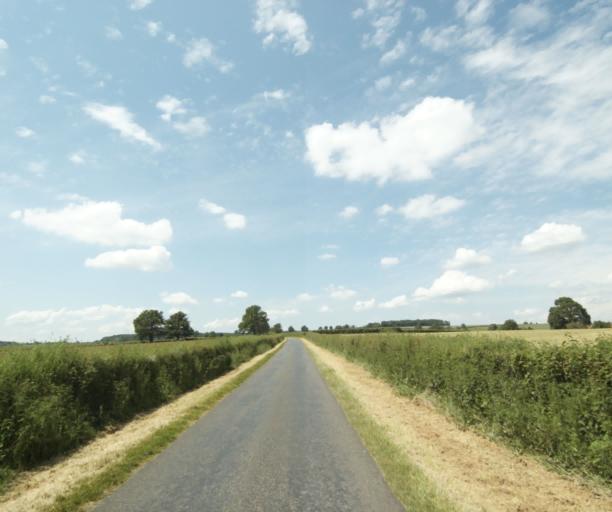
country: FR
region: Bourgogne
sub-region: Departement de Saone-et-Loire
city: Perrecy-les-Forges
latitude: 46.5816
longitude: 4.1477
